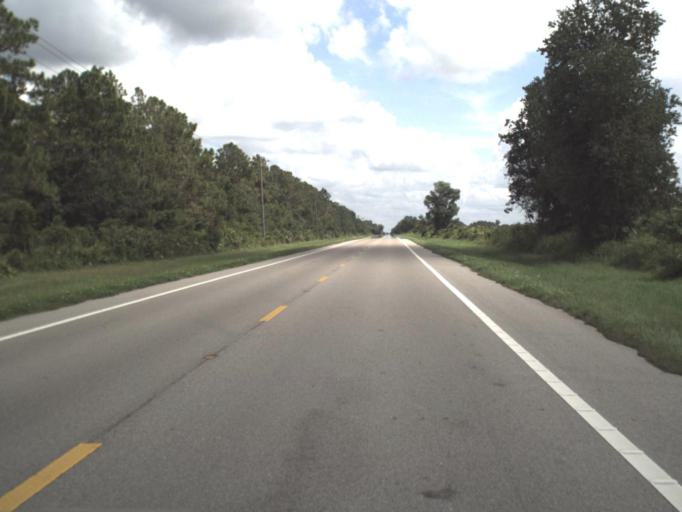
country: US
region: Florida
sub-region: Hillsborough County
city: Wimauma
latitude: 27.4597
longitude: -82.1649
